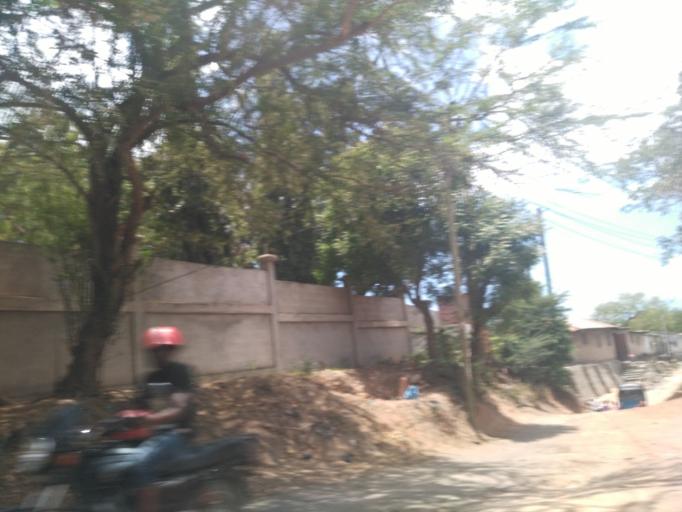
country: TZ
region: Dar es Salaam
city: Dar es Salaam
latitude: -6.8596
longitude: 39.2690
